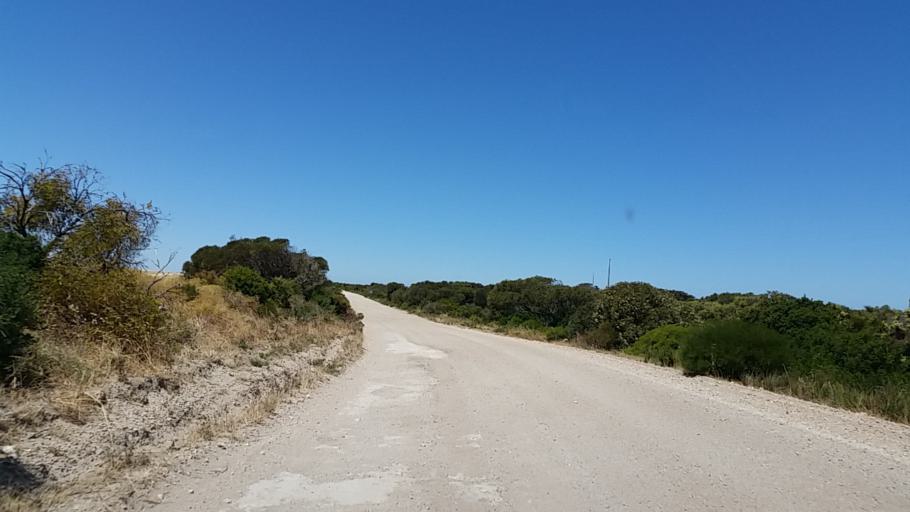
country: AU
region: South Australia
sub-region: Yorke Peninsula
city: Honiton
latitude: -35.1172
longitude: 137.3705
